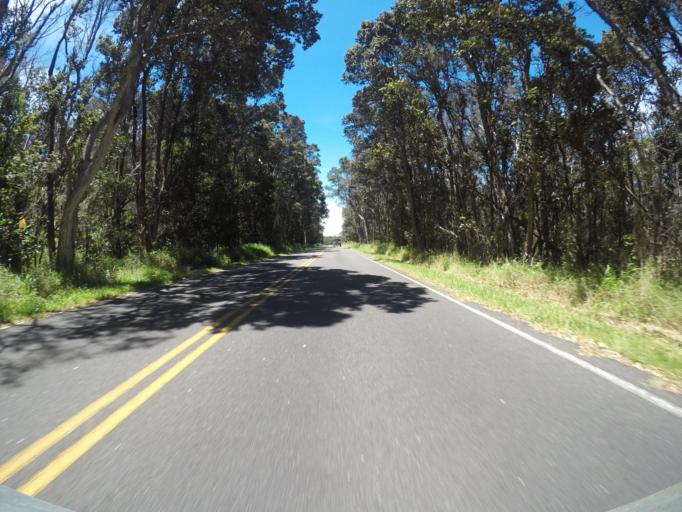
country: US
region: Hawaii
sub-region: Hawaii County
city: Volcano
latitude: 19.4016
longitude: -155.2534
